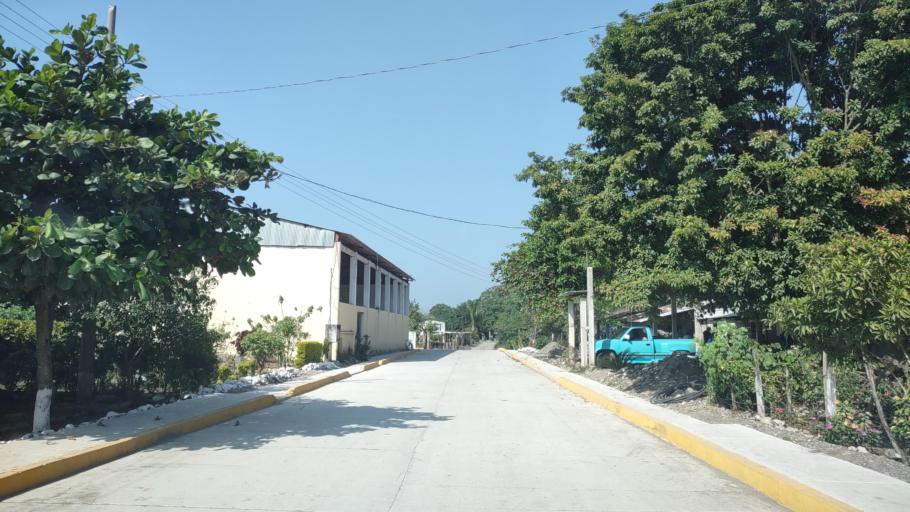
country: MX
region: Veracruz
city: Agua Dulce
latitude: 20.2751
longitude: -97.2852
